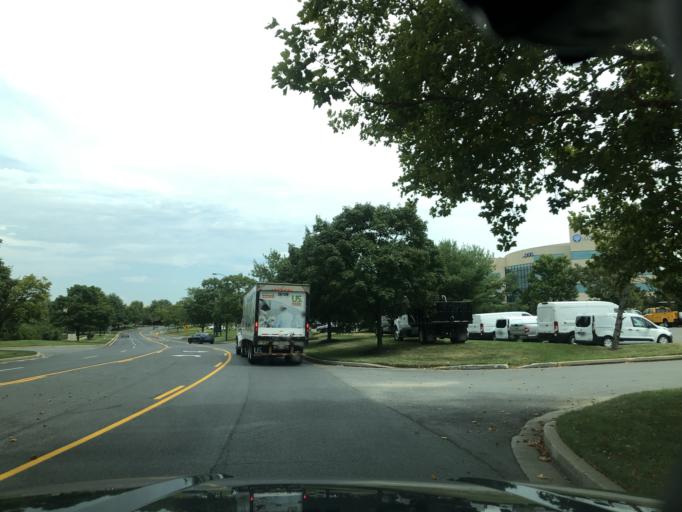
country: US
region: Maryland
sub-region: Howard County
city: Savage
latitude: 39.1887
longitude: -76.8173
